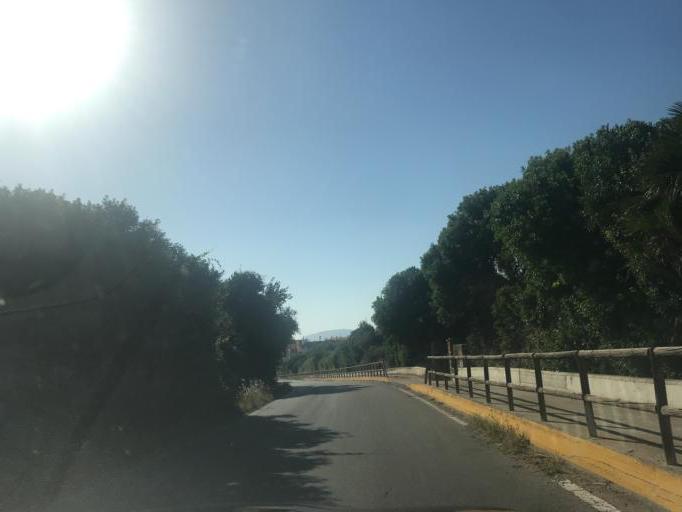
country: IT
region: Sardinia
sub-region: Provincia di Sassari
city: Alghero
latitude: 40.5545
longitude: 8.3328
